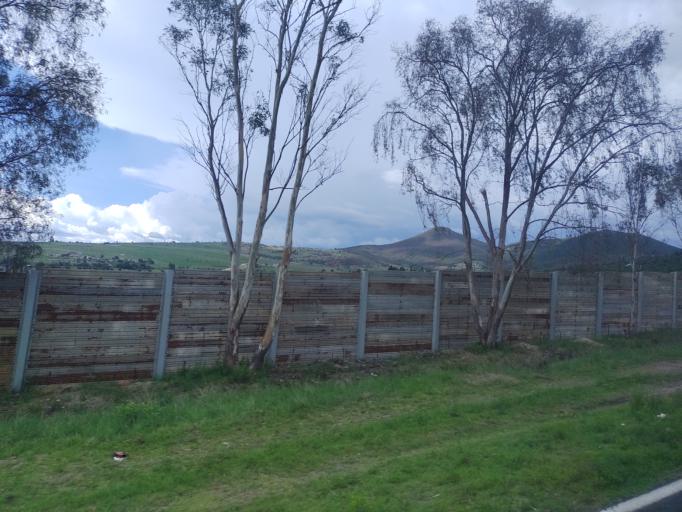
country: MX
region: Mexico
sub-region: Aculco
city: El Colorado
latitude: 20.1042
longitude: -99.7063
